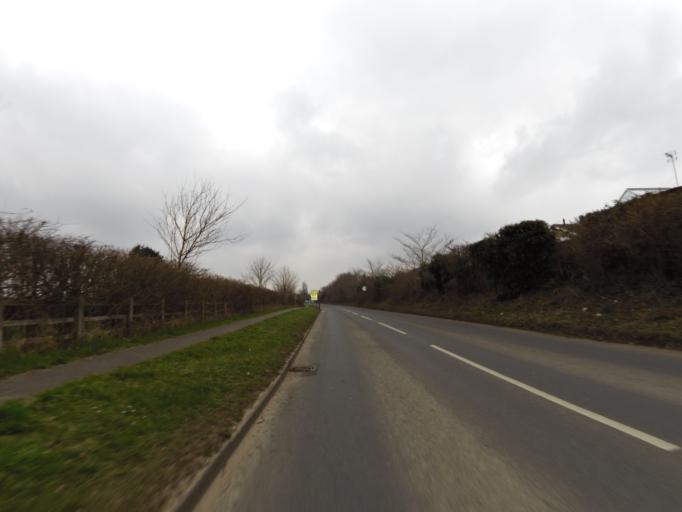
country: GB
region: England
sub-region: Suffolk
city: Wickham Market
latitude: 52.1571
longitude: 1.3618
